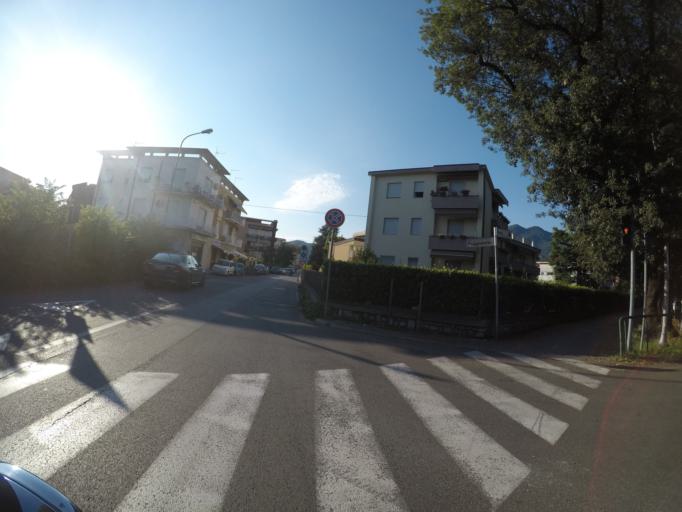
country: IT
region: Tuscany
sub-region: Provincia di Massa-Carrara
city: Massa
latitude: 44.0290
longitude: 10.1328
